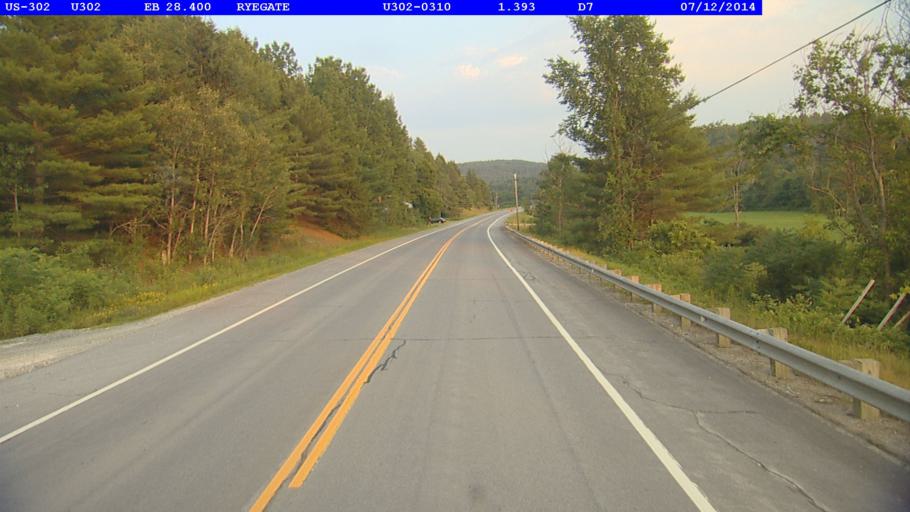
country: US
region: New Hampshire
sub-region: Grafton County
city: Woodsville
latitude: 44.1940
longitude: -72.1487
